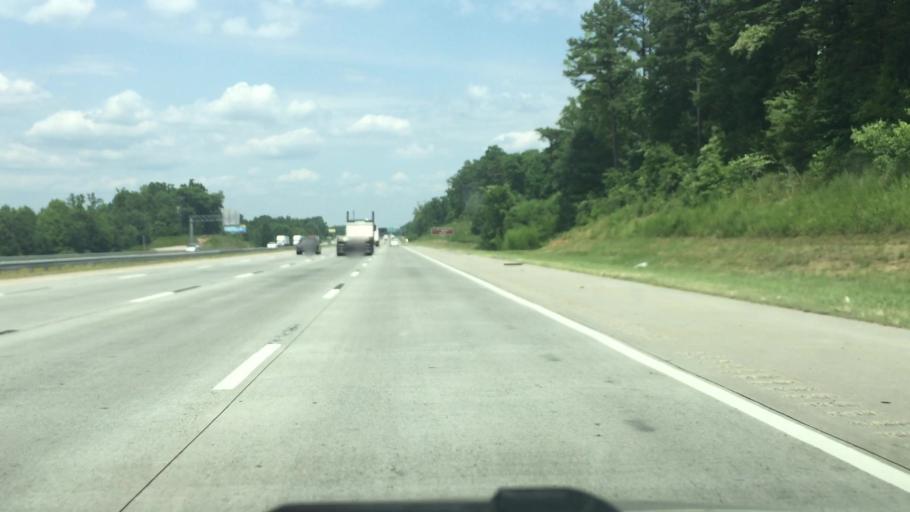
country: US
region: North Carolina
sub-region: Rowan County
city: East Spencer
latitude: 35.6665
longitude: -80.4425
